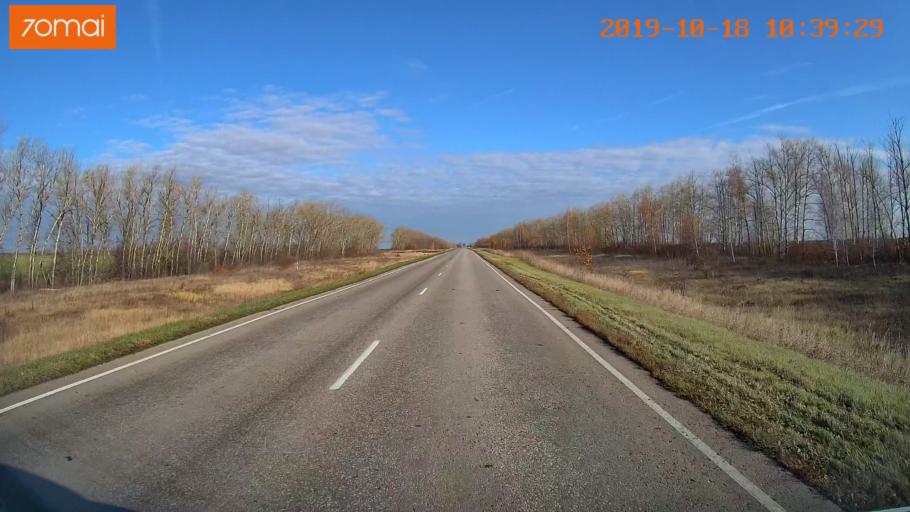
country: RU
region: Tula
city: Kurkino
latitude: 53.5875
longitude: 38.6534
